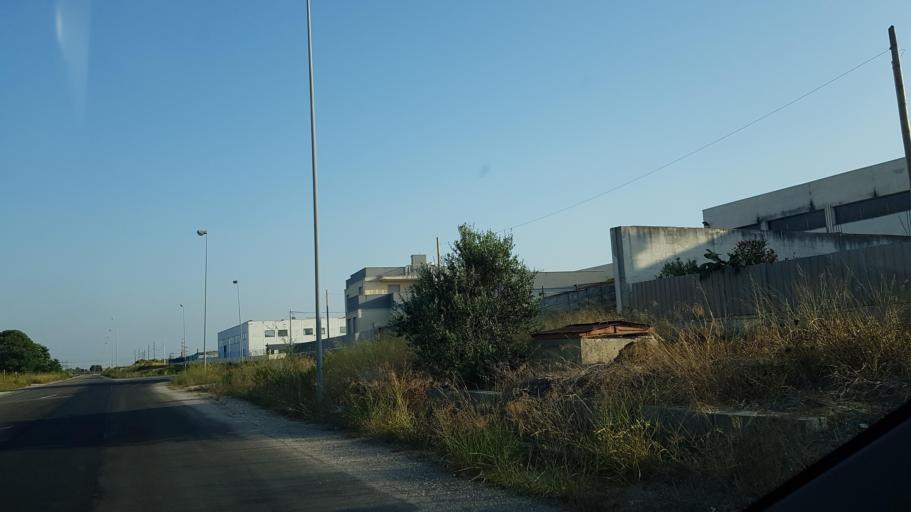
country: IT
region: Apulia
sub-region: Provincia di Brindisi
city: Materdomini
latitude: 40.6285
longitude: 17.9759
